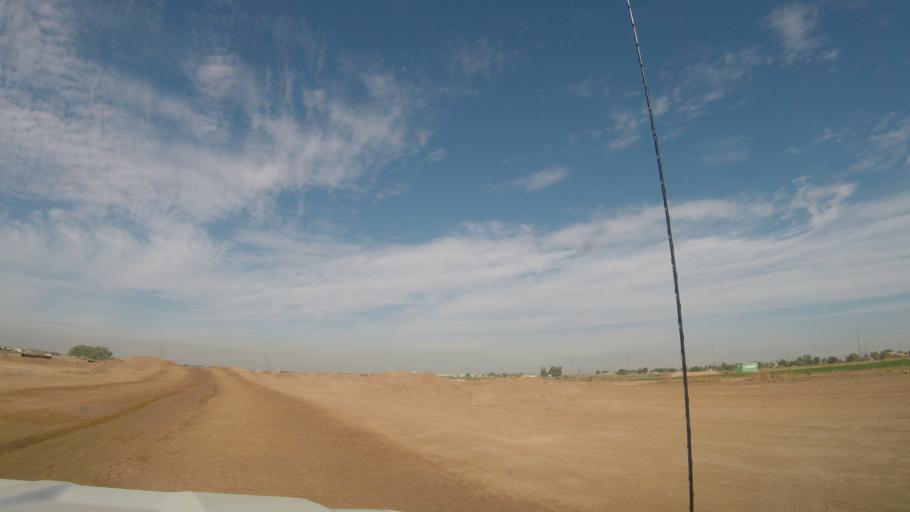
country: US
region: Arizona
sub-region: Maricopa County
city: Laveen
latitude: 33.3836
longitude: -112.1902
